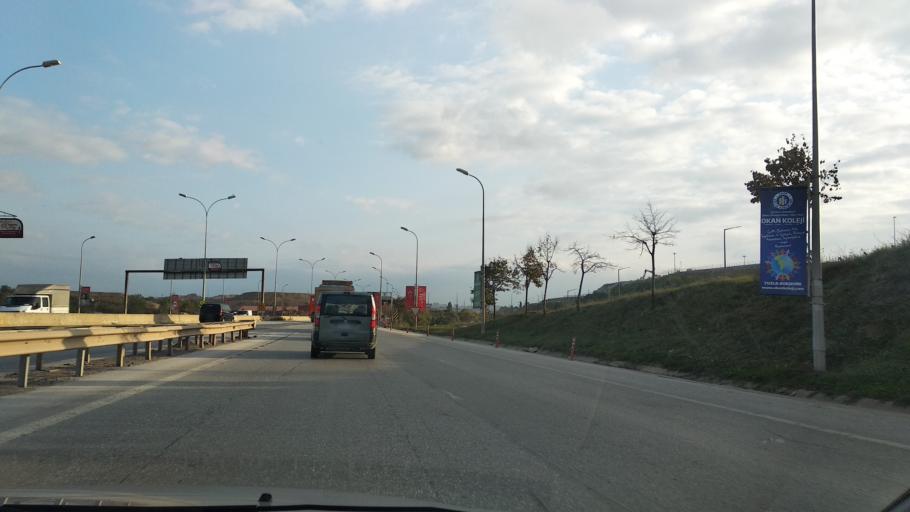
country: TR
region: Istanbul
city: Pendik
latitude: 40.9117
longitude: 29.3260
